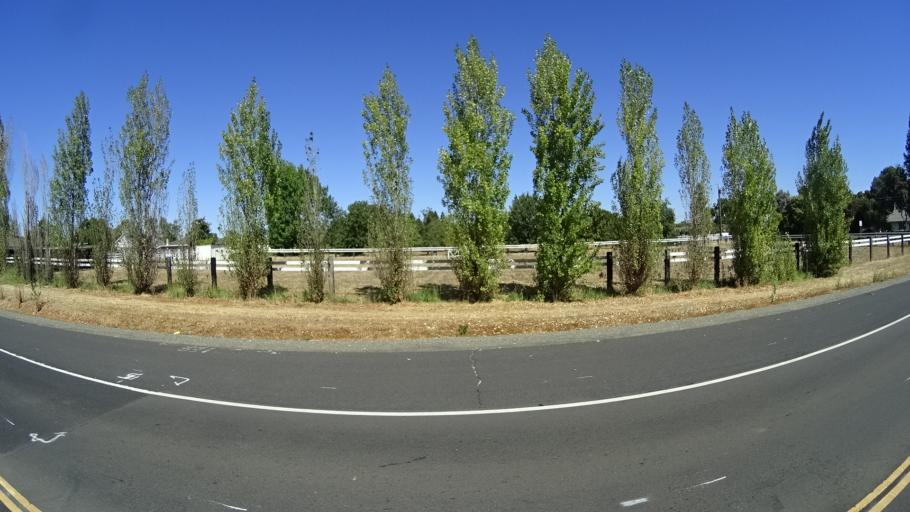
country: US
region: California
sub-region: Sacramento County
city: Vineyard
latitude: 38.4381
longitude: -121.3582
